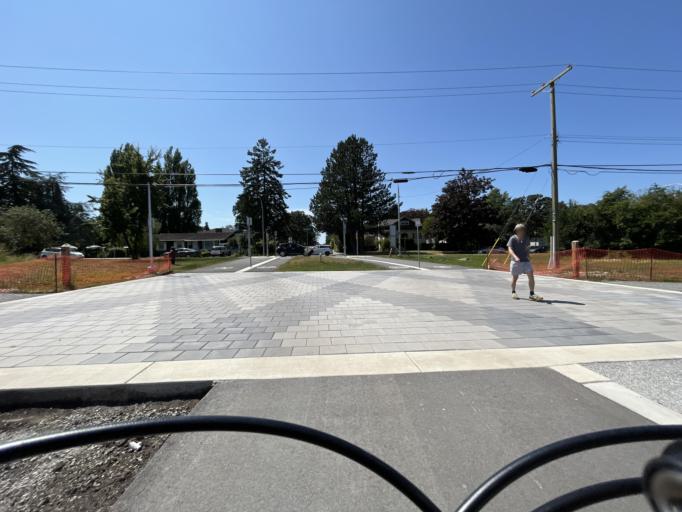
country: CA
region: British Columbia
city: Oak Bay
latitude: 48.4636
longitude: -123.3203
